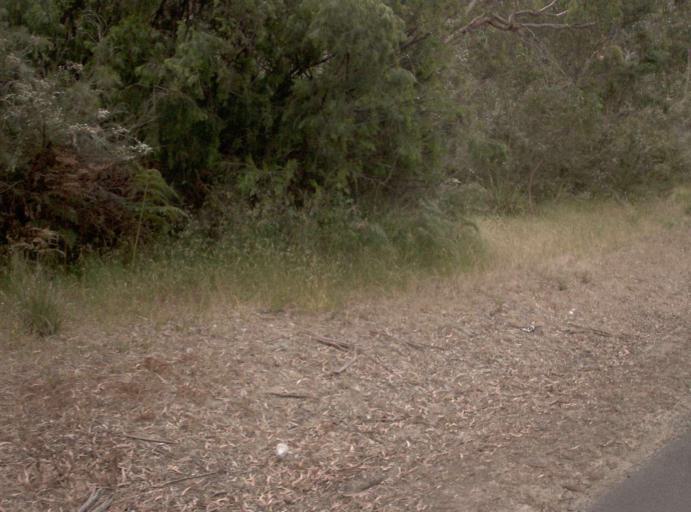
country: AU
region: Victoria
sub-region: Wellington
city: Sale
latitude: -38.2475
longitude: 147.0555
